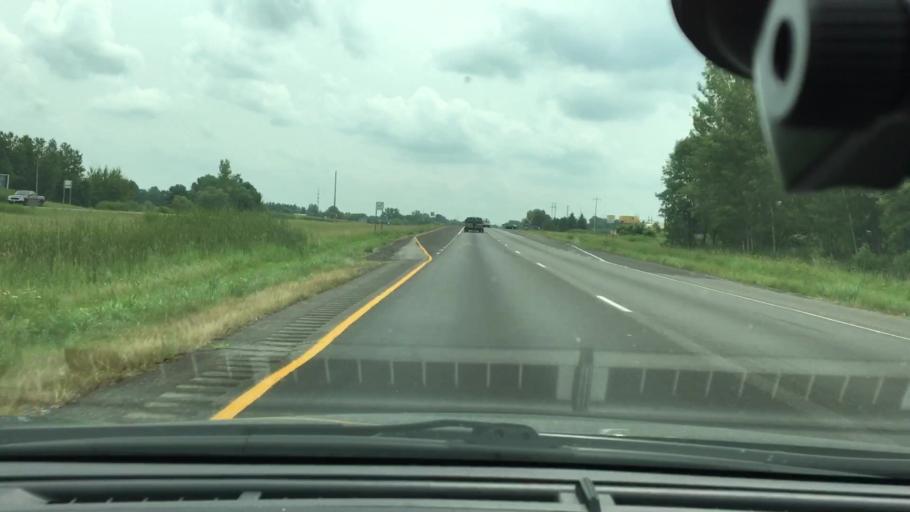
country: US
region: Minnesota
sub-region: Mille Lacs County
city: Princeton
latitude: 45.6074
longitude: -93.6063
